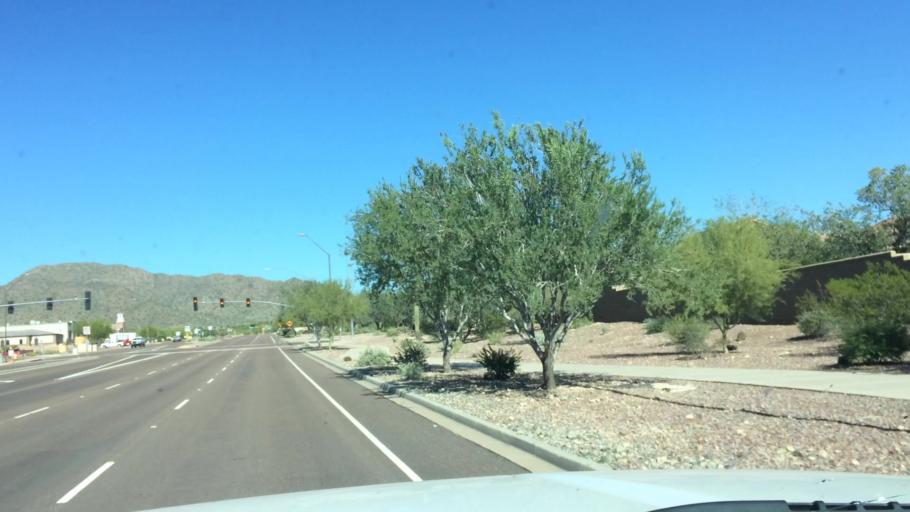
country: US
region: Arizona
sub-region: Maricopa County
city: Anthem
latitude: 33.8556
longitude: -112.1147
